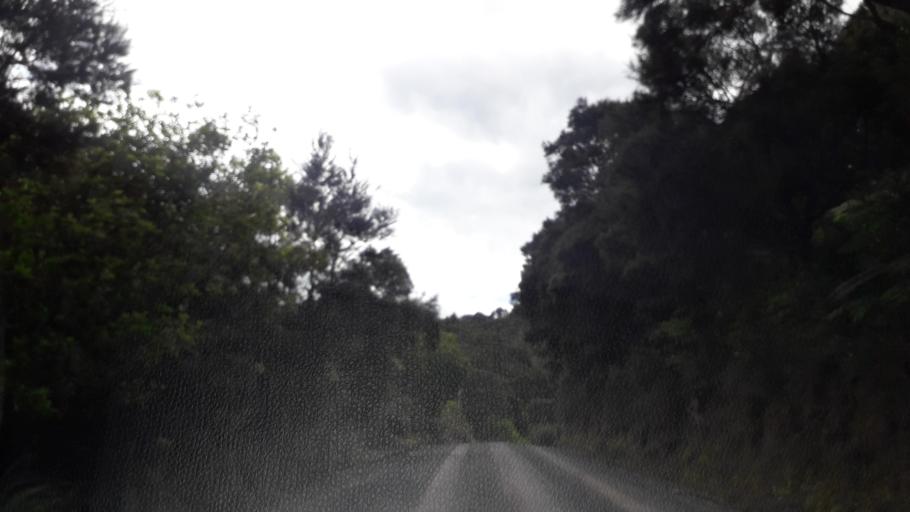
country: NZ
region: Northland
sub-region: Far North District
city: Paihia
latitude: -35.3073
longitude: 174.2203
